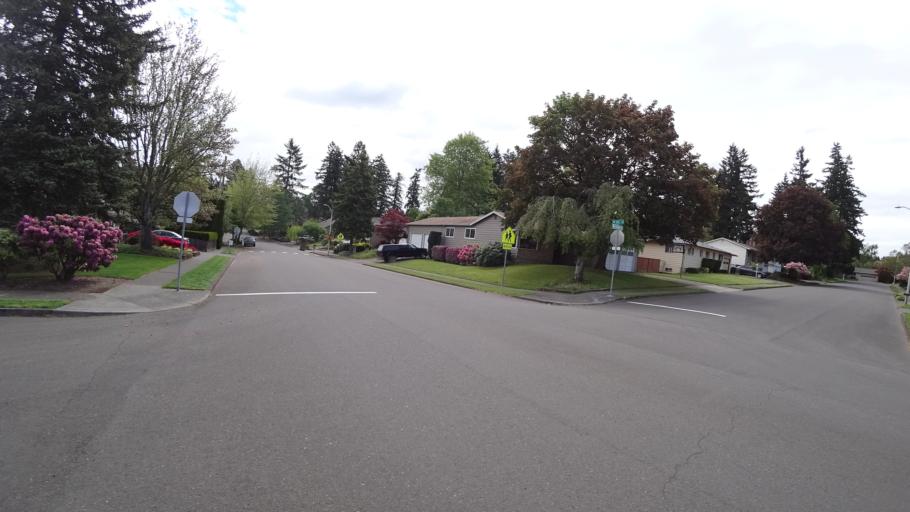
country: US
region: Oregon
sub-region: Washington County
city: Beaverton
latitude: 45.4720
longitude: -122.8164
